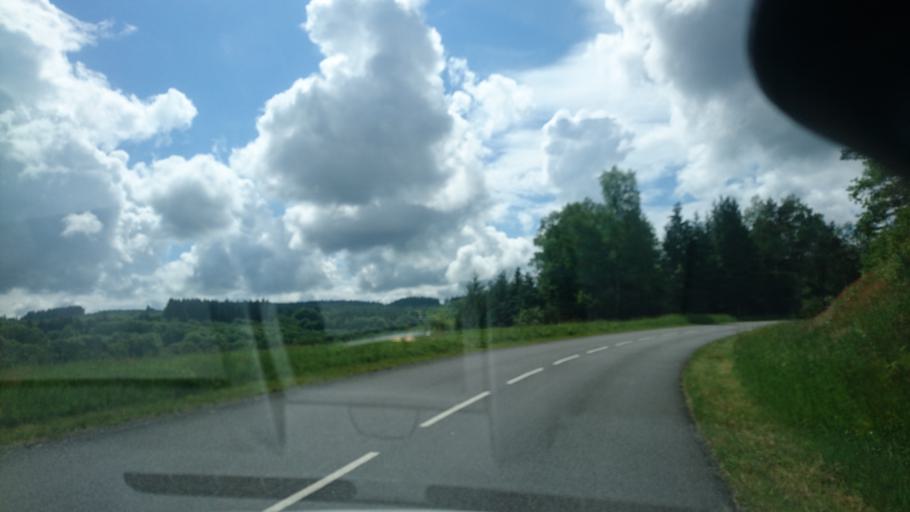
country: FR
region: Limousin
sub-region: Departement de la Haute-Vienne
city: Peyrat-le-Chateau
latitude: 45.7802
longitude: 1.8657
